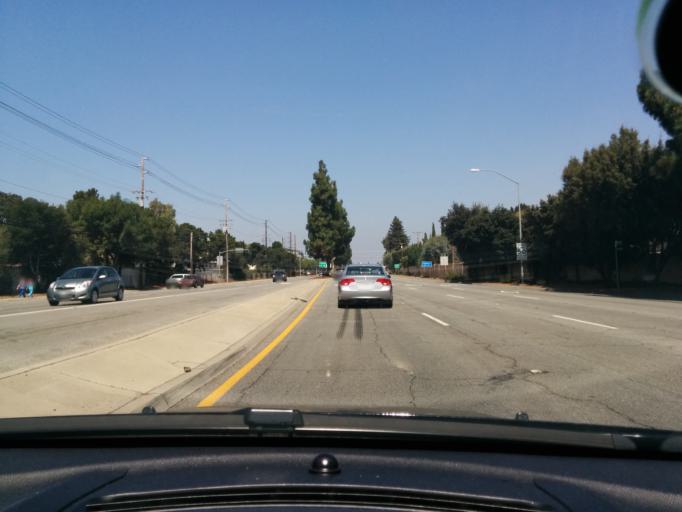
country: US
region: California
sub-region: Santa Clara County
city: Cupertino
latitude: 37.3319
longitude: -121.9955
